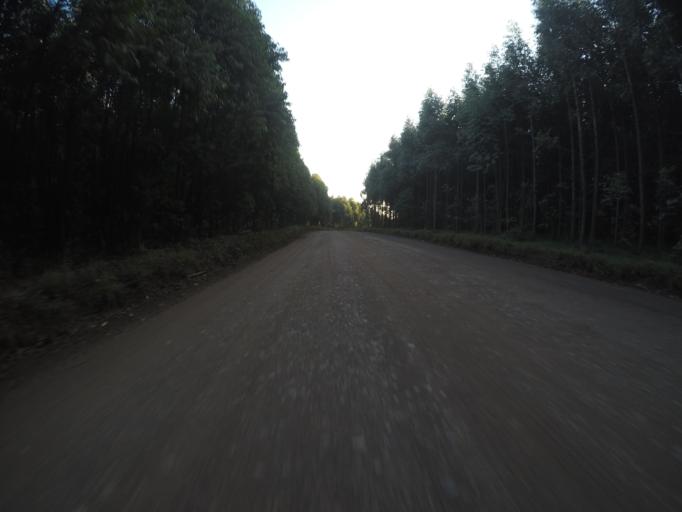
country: ZA
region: KwaZulu-Natal
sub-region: uThungulu District Municipality
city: KwaMbonambi
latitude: -28.6766
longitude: 32.1185
